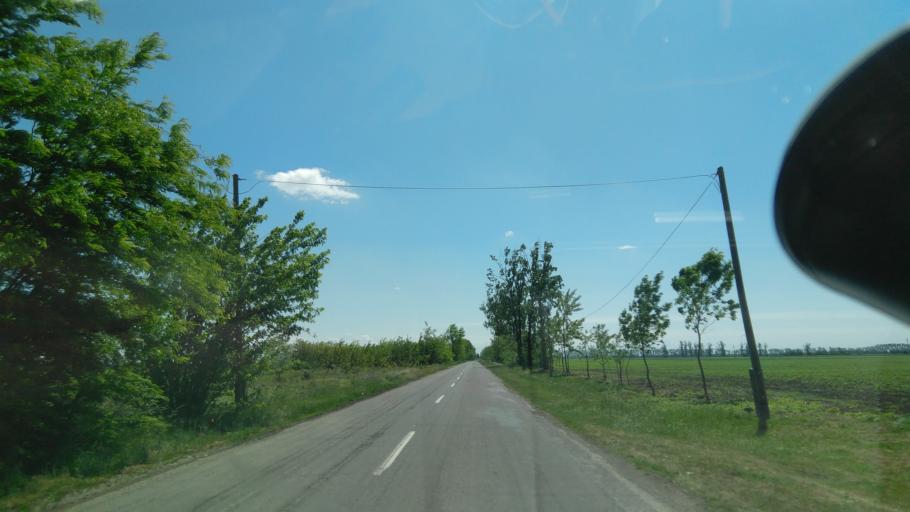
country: HU
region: Bekes
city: Kunagota
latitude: 46.4135
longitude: 21.0459
